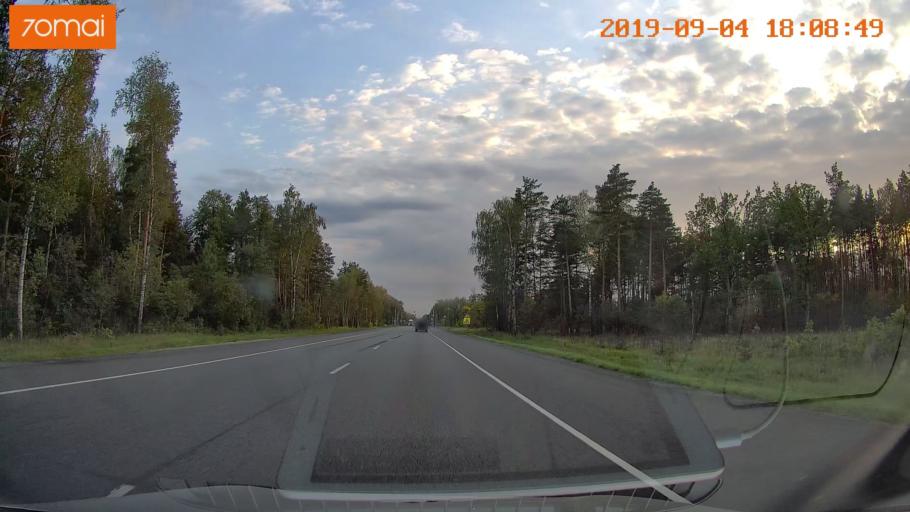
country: RU
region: Moskovskaya
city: Khorlovo
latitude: 55.4014
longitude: 38.7808
